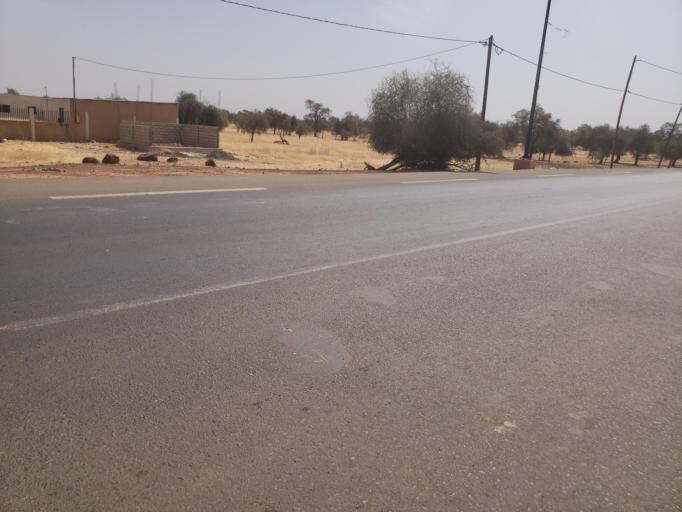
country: SN
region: Matam
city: Ranerou
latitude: 15.2965
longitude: -13.9573
